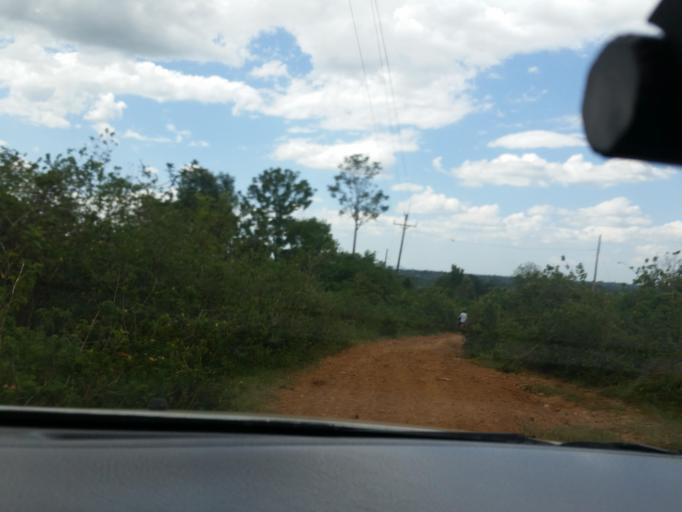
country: KE
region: Kakamega
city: Butere
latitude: 0.1110
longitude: 34.4086
